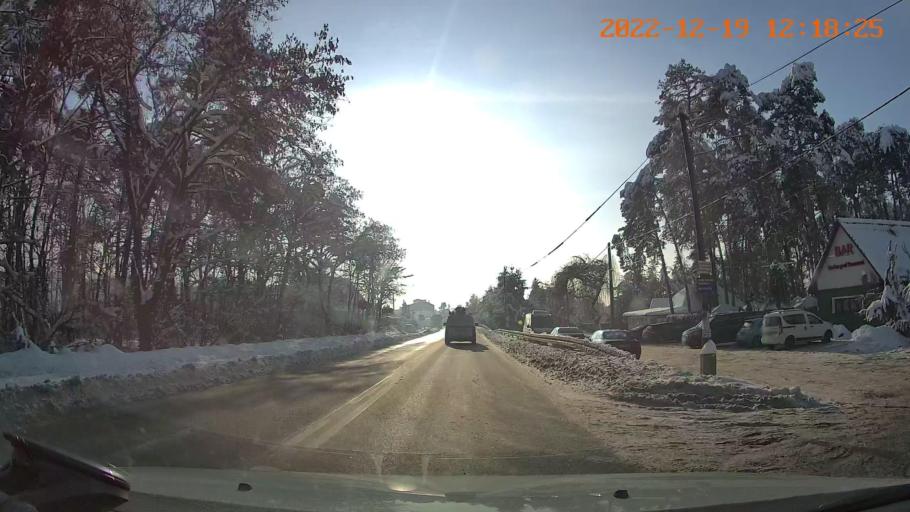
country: PL
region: Lesser Poland Voivodeship
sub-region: Powiat krakowski
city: Kryspinow
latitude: 50.0490
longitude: 19.7992
